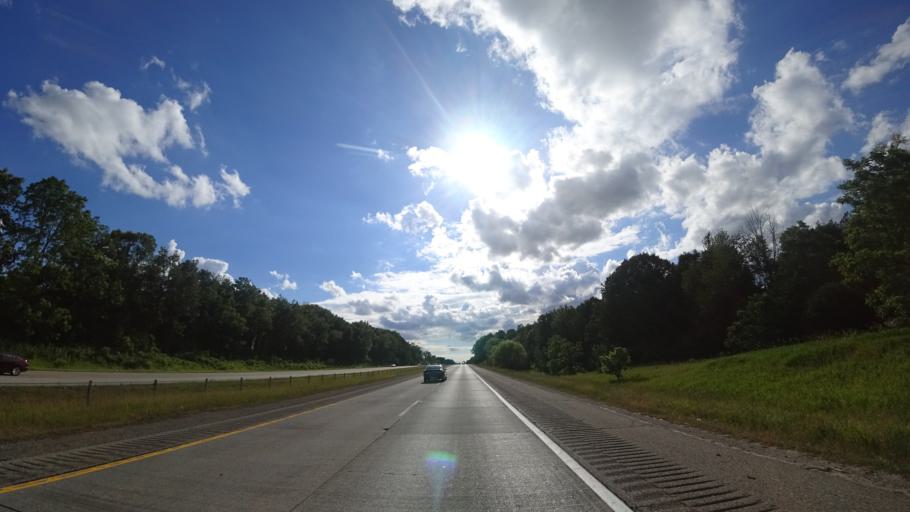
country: US
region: Michigan
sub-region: Kent County
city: Lowell
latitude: 42.8788
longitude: -85.3813
